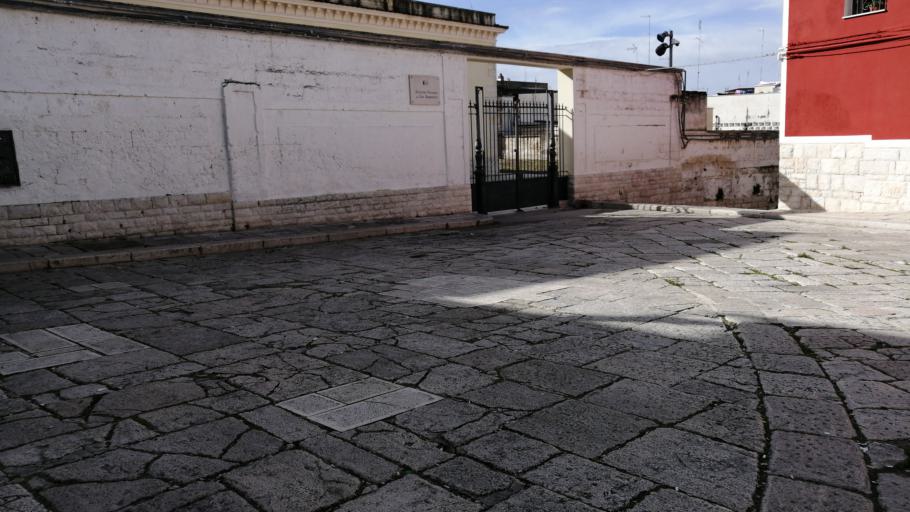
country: IT
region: Apulia
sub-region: Provincia di Barletta - Andria - Trani
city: Andria
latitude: 41.2258
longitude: 16.2941
